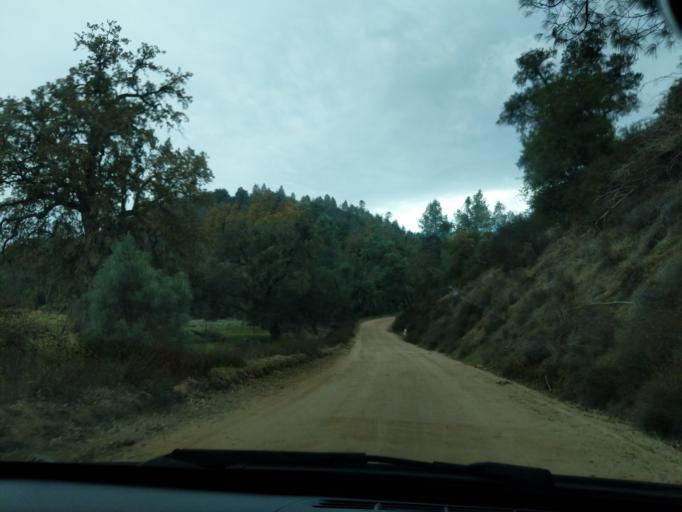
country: US
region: California
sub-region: Monterey County
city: Soledad
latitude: 36.5599
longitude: -121.2361
